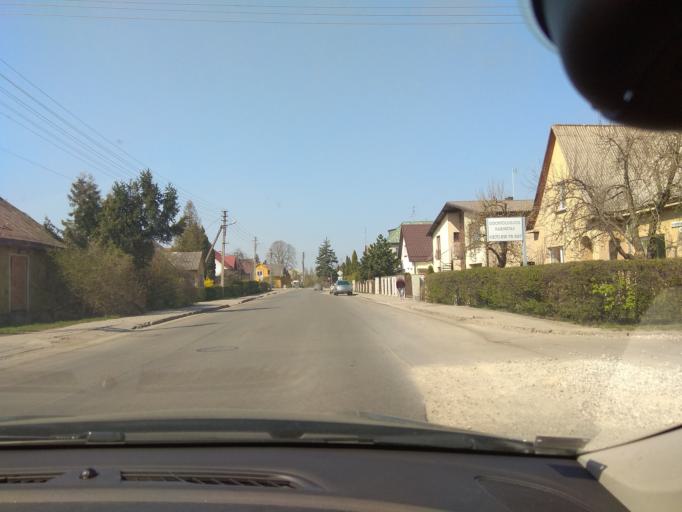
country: LT
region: Marijampoles apskritis
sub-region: Marijampole Municipality
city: Marijampole
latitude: 54.5641
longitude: 23.3517
